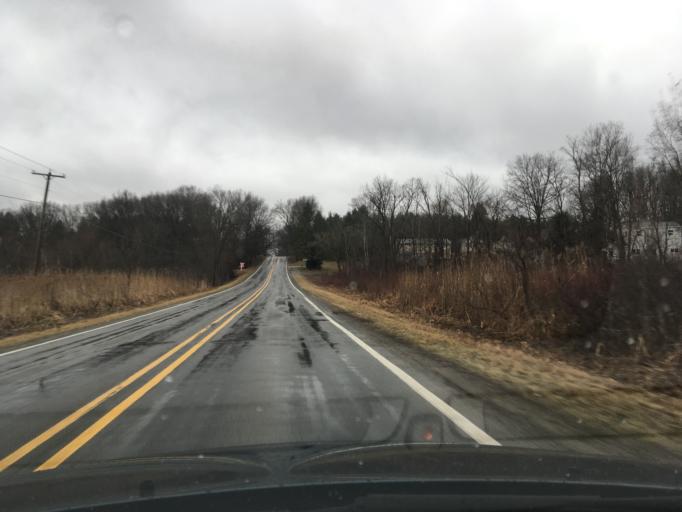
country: US
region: Michigan
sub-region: Washtenaw County
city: Chelsea
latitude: 42.3091
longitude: -84.0754
